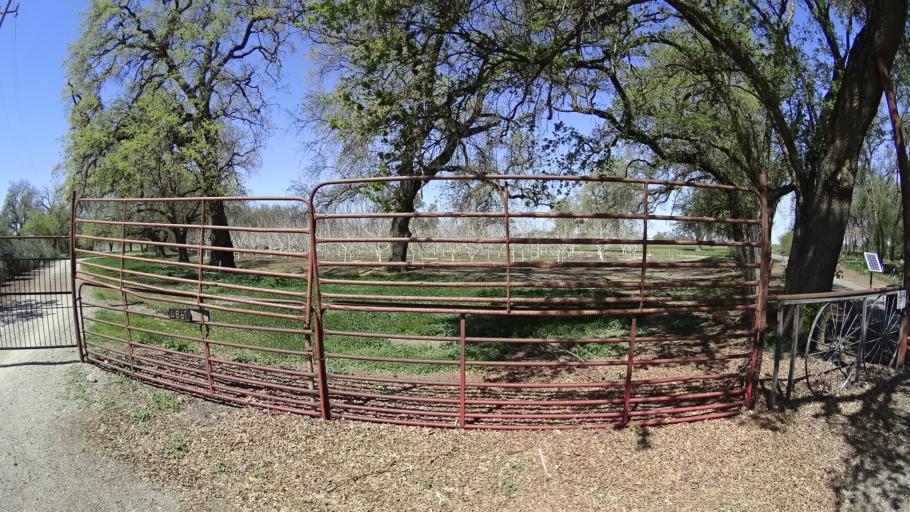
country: US
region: California
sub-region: Glenn County
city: Orland
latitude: 39.7866
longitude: -122.2760
